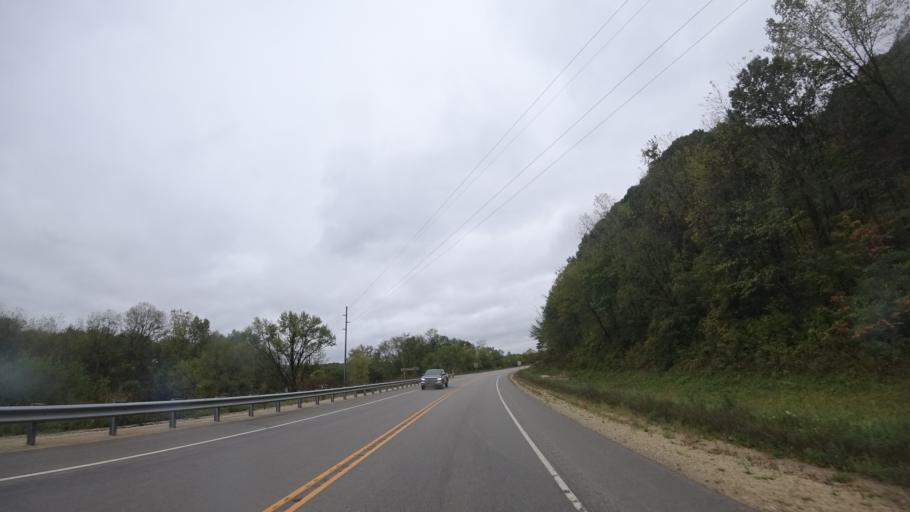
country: US
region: Wisconsin
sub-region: Grant County
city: Boscobel
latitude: 43.1668
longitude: -90.7055
